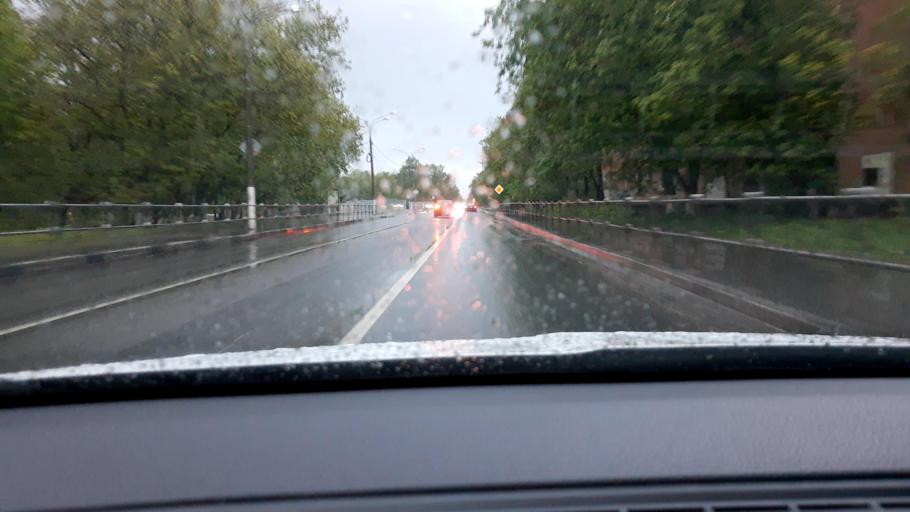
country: RU
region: Moskovskaya
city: Shchelkovo
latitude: 55.9250
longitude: 37.9639
